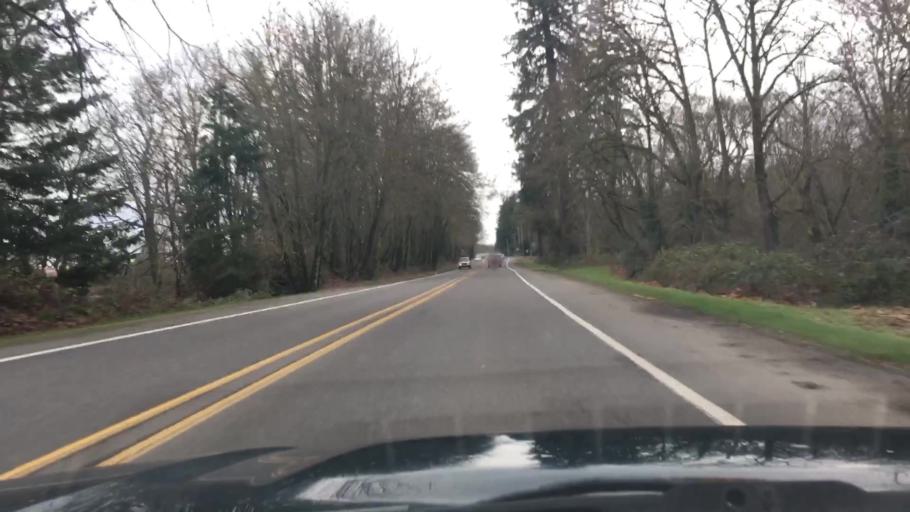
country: US
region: Oregon
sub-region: Lane County
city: Coburg
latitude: 44.1100
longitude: -123.0492
